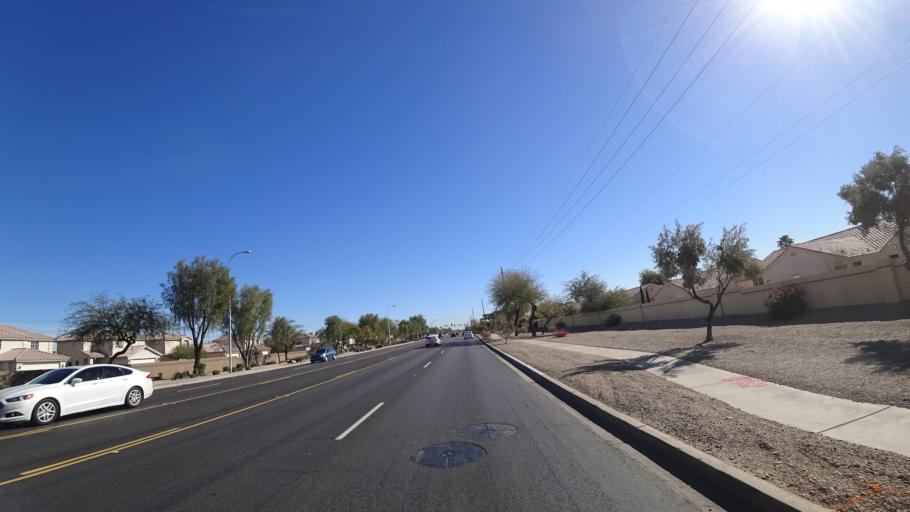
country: US
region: Arizona
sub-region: Maricopa County
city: Litchfield Park
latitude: 33.4932
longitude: -112.3014
